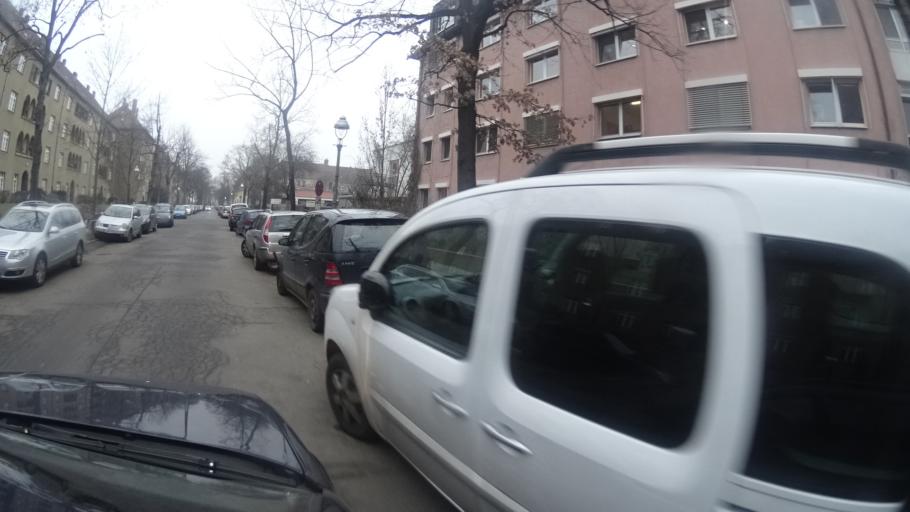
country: DE
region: Berlin
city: Schoneberg Bezirk
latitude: 52.4776
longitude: 13.3713
